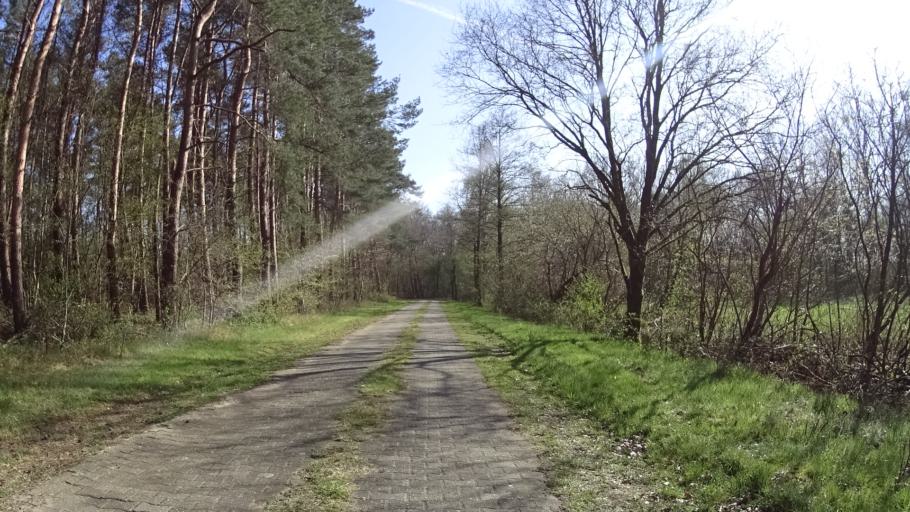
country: DE
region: Lower Saxony
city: Lehe
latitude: 52.9896
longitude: 7.3230
